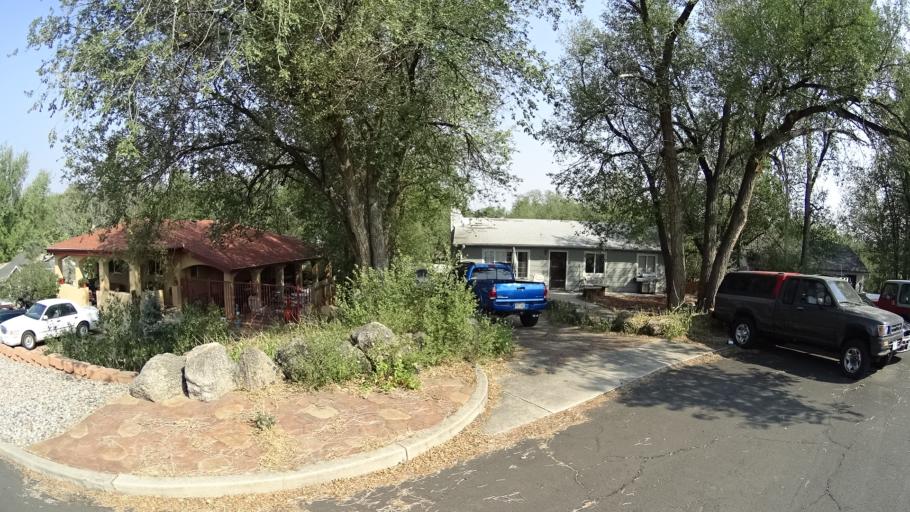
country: US
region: Colorado
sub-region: El Paso County
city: Colorado Springs
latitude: 38.8109
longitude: -104.8323
